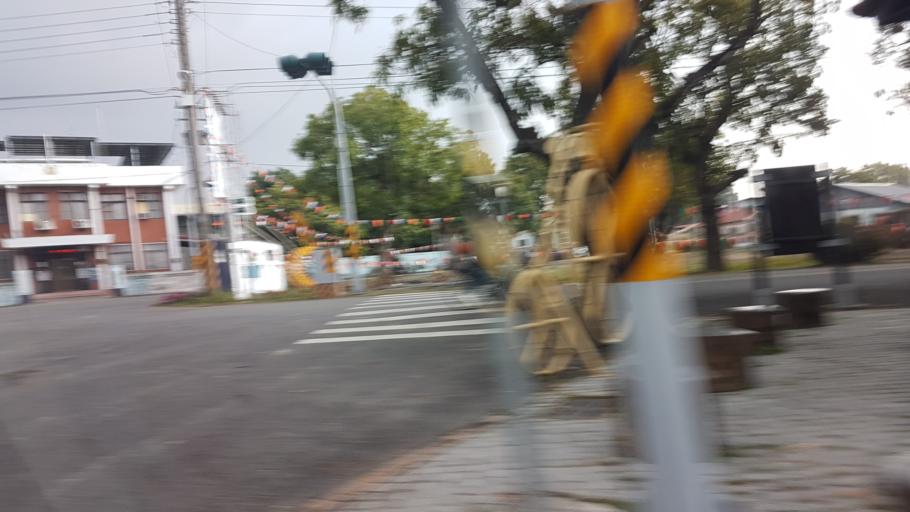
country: TW
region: Taiwan
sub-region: Chiayi
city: Jiayi Shi
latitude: 23.3767
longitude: 120.4445
